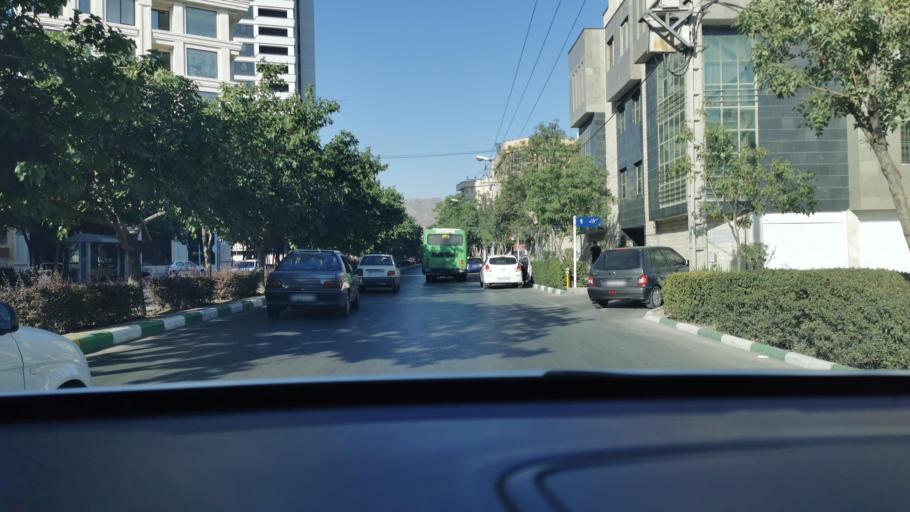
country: IR
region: Razavi Khorasan
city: Mashhad
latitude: 36.3156
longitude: 59.5191
